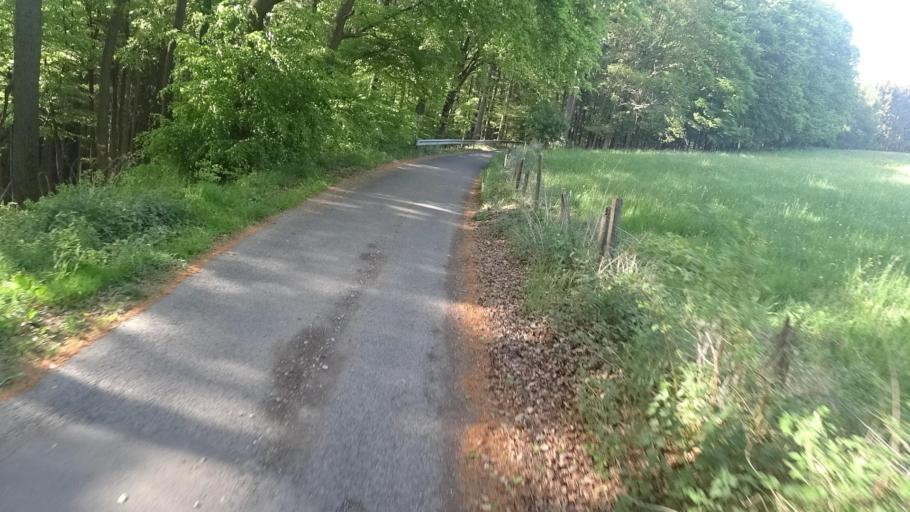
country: DE
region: Rheinland-Pfalz
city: Kirchsahr
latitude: 50.5101
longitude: 6.8699
